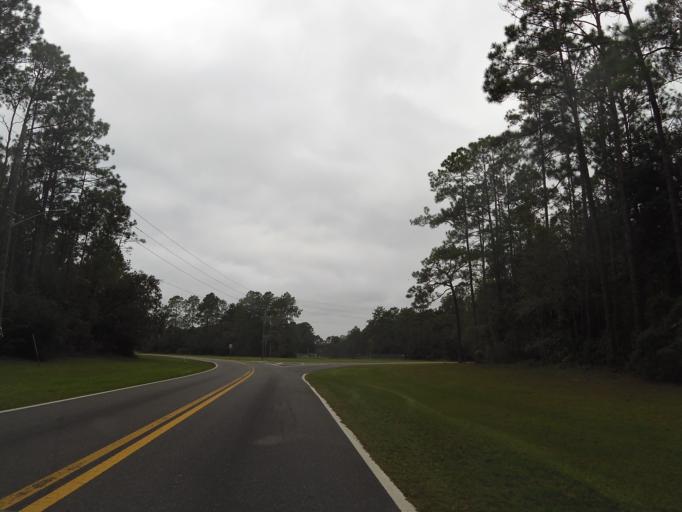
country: US
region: Florida
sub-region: Duval County
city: Baldwin
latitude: 30.2255
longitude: -81.8928
